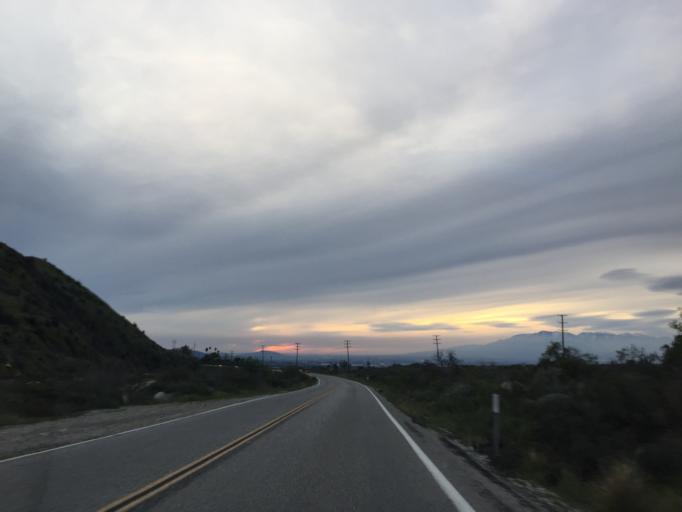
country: US
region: California
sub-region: San Bernardino County
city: Yucaipa
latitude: 34.0763
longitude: -117.0609
